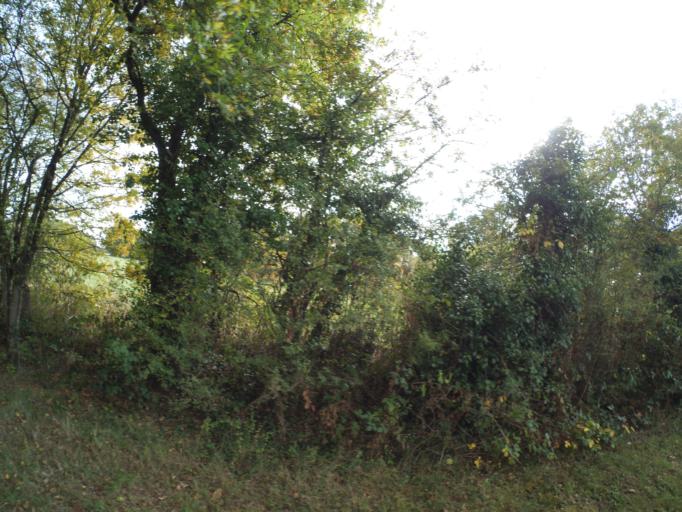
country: FR
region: Pays de la Loire
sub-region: Departement de la Loire-Atlantique
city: Saint-Lumine-de-Clisson
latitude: 47.0728
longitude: -1.3515
